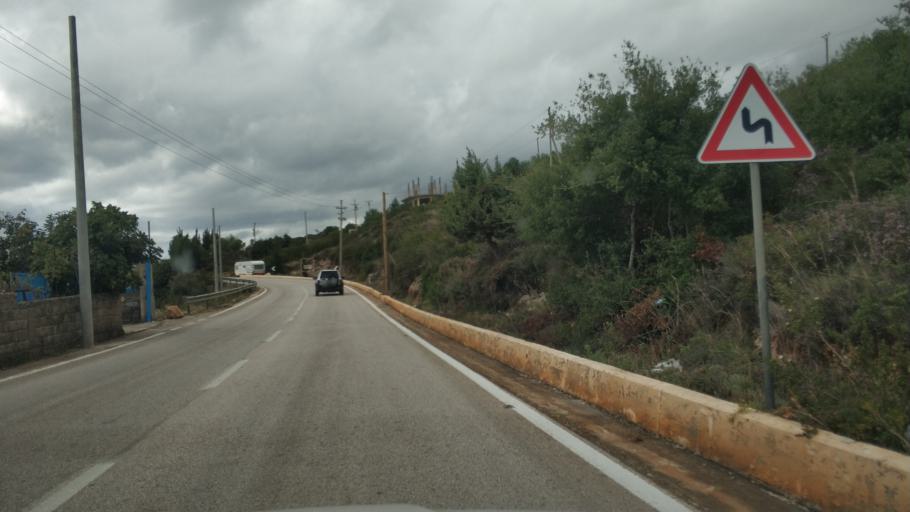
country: AL
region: Vlore
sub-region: Rrethi i Vlores
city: Vranisht
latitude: 40.1451
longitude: 19.6461
